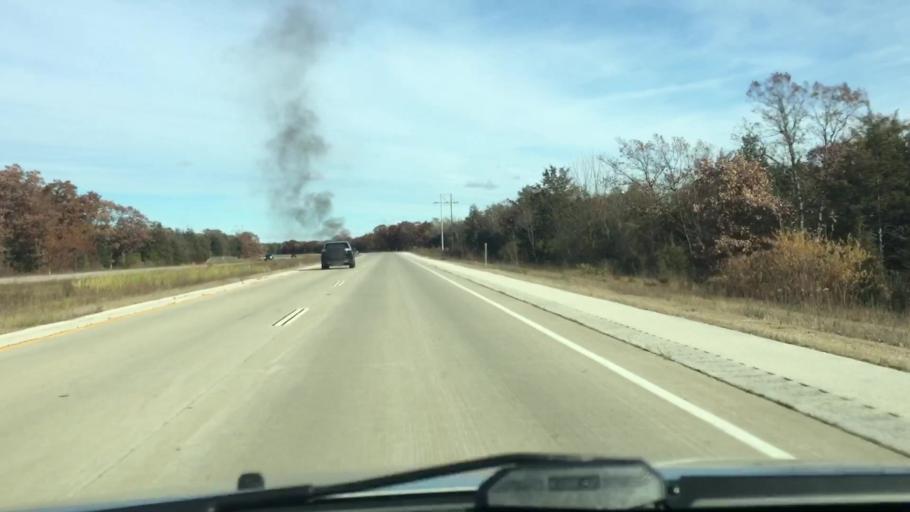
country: US
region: Wisconsin
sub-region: Kewaunee County
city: Luxemburg
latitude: 44.6099
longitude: -87.8428
